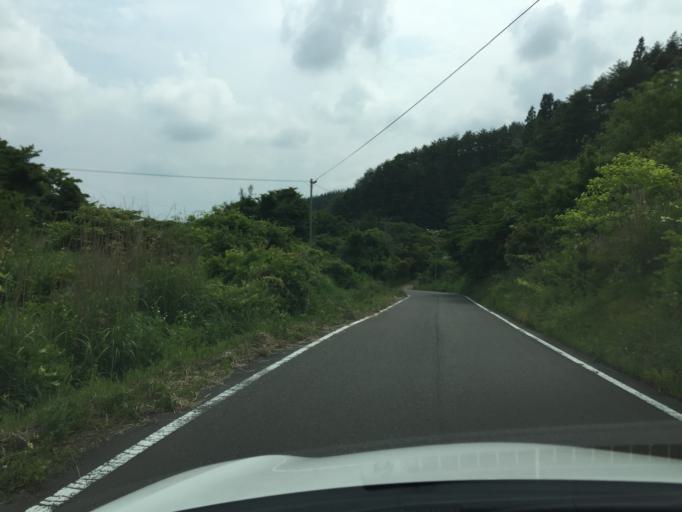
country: JP
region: Fukushima
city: Ishikawa
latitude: 37.2554
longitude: 140.4981
